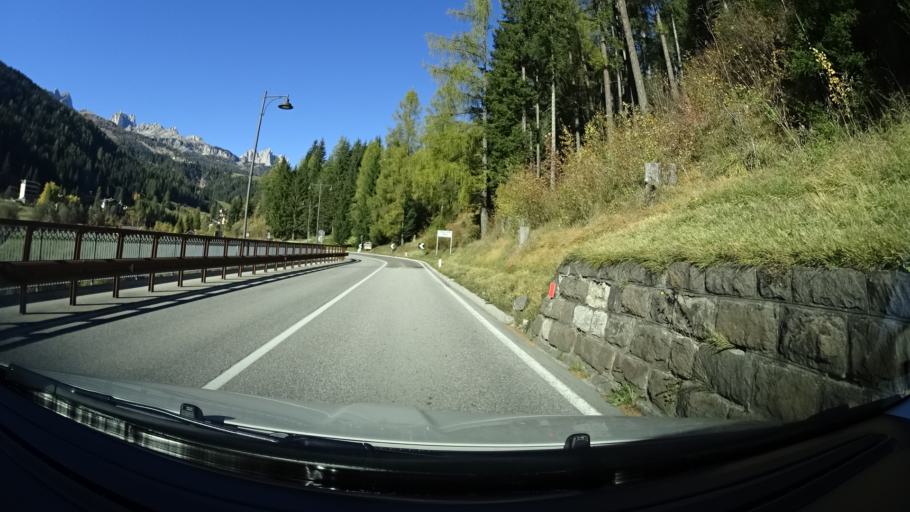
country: IT
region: Trentino-Alto Adige
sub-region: Provincia di Trento
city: Soraga
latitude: 46.3890
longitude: 11.6677
